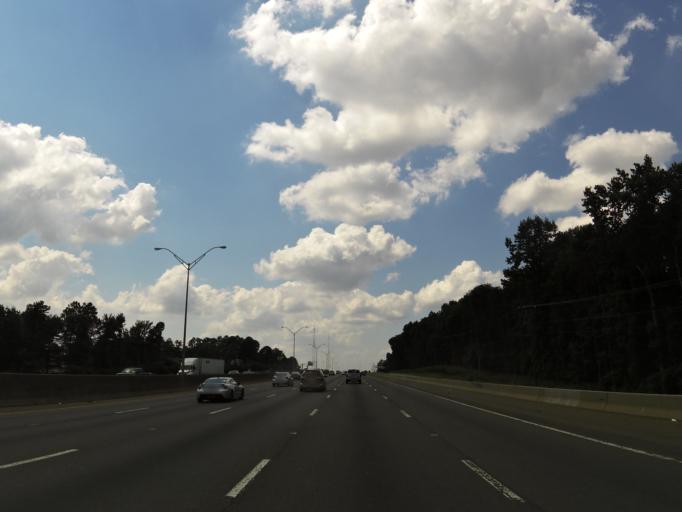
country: US
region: North Carolina
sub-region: Mecklenburg County
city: Charlotte
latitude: 35.2814
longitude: -80.7840
